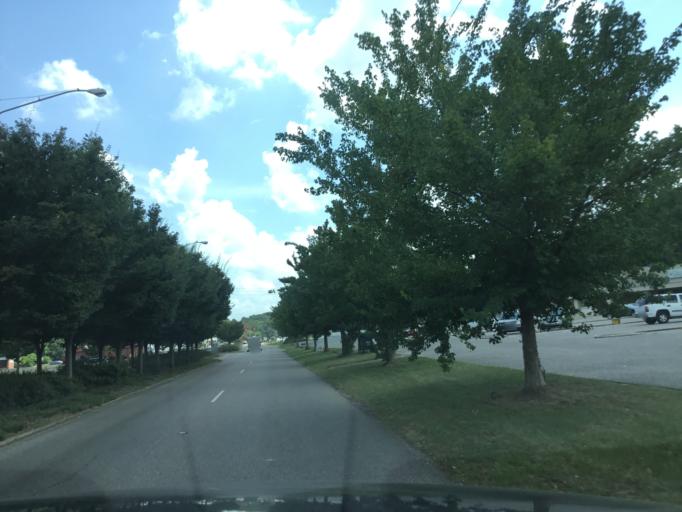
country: US
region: Alabama
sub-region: Montgomery County
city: Montgomery
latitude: 32.3909
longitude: -86.2575
